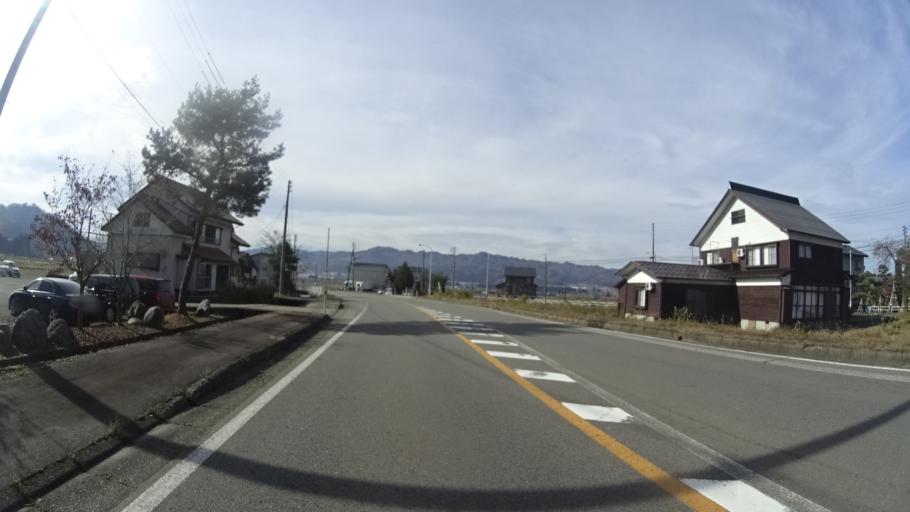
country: JP
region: Niigata
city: Muikamachi
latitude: 37.1290
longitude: 138.9394
